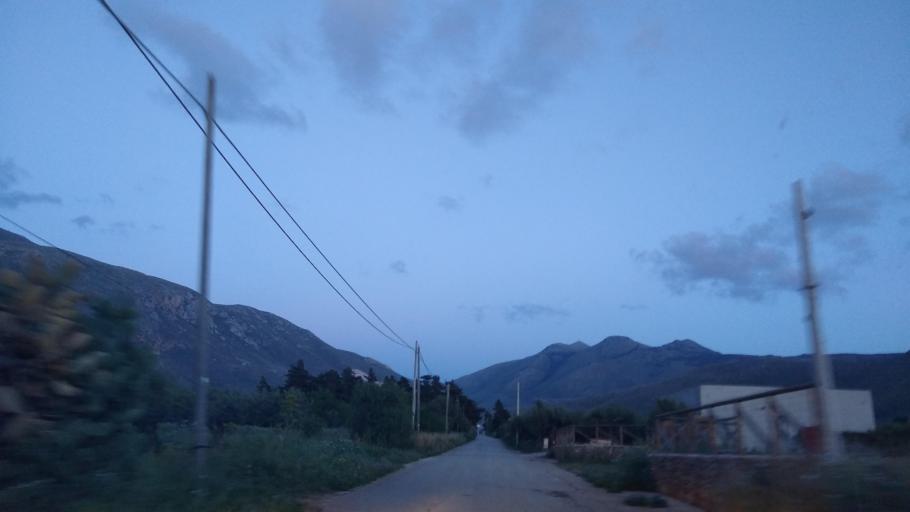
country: IT
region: Sicily
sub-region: Trapani
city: Castelluzzo
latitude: 38.1074
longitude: 12.7283
